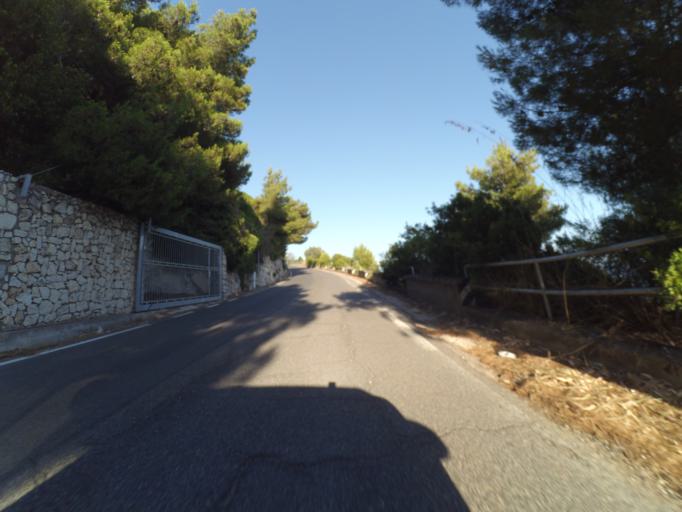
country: IT
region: Latium
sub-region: Provincia di Latina
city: San Felice Circeo
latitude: 41.2248
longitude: 13.0829
